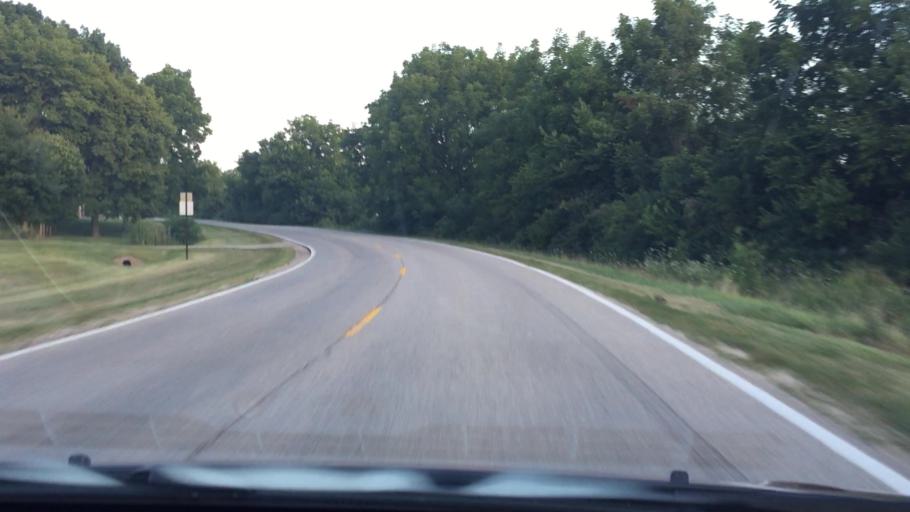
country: US
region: Iowa
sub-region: Muscatine County
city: Muscatine
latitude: 41.4514
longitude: -91.0593
